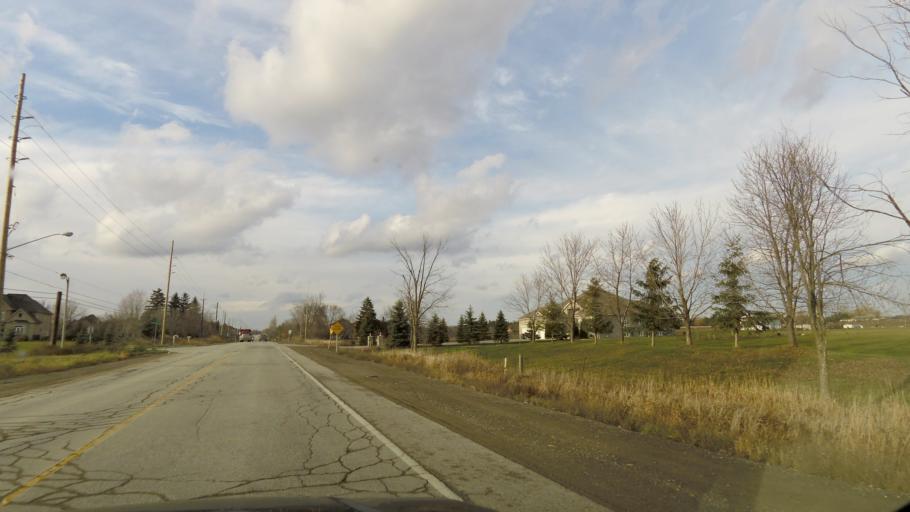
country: CA
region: Ontario
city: Brampton
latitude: 43.8093
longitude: -79.7134
